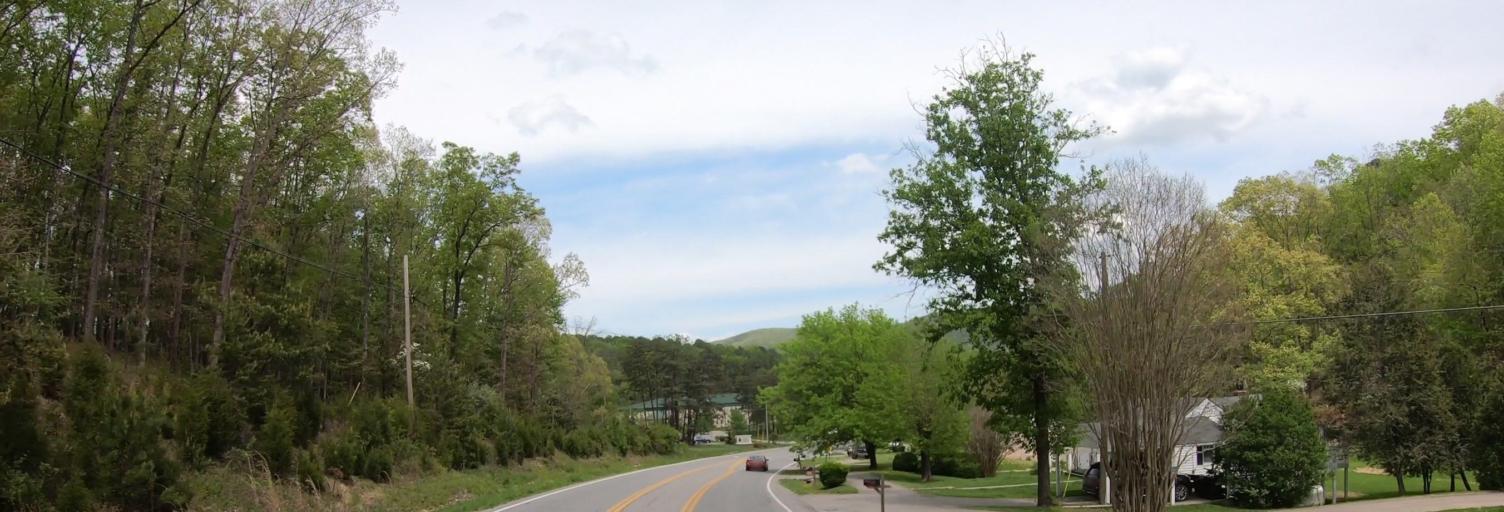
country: US
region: Virginia
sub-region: Roanoke County
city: Narrows
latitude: 37.2045
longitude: -79.9640
